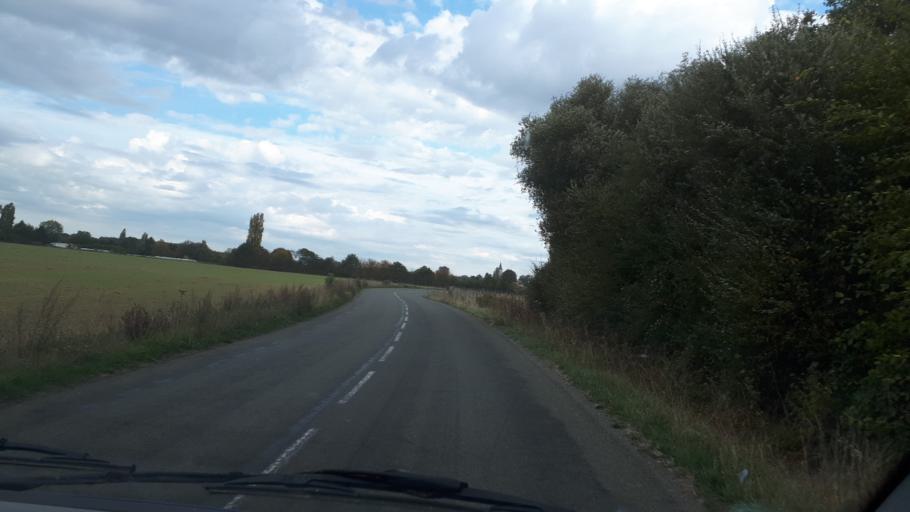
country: FR
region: Centre
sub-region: Departement d'Eure-et-Loir
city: Authon-du-Perche
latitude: 48.1902
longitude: 0.9059
